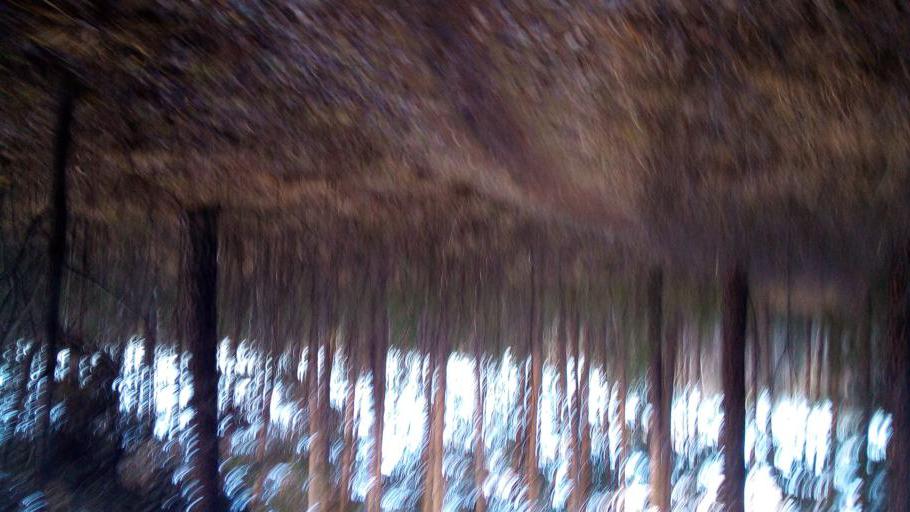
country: RU
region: Chelyabinsk
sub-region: Gorod Chelyabinsk
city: Chelyabinsk
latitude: 55.1589
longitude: 61.3452
